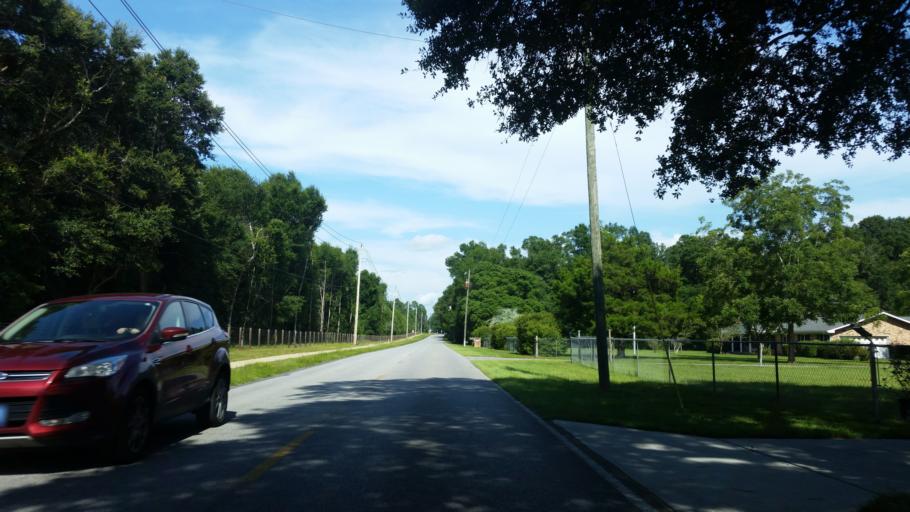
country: US
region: Florida
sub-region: Santa Rosa County
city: Pace
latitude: 30.6181
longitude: -87.1372
